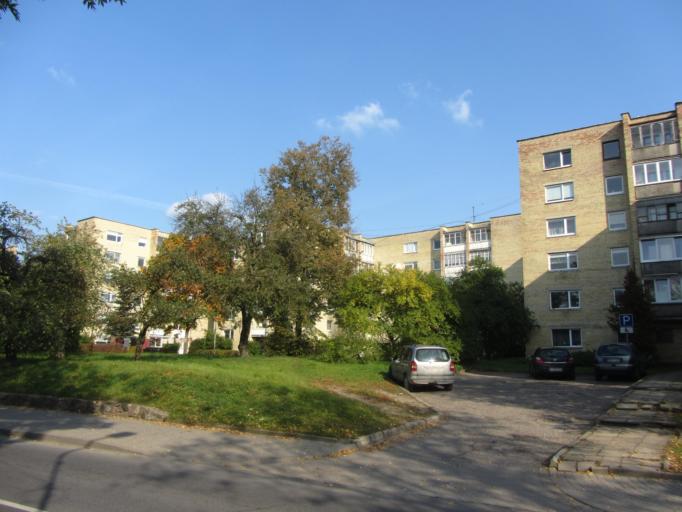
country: LT
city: Trakai
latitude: 54.6349
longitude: 24.9340
